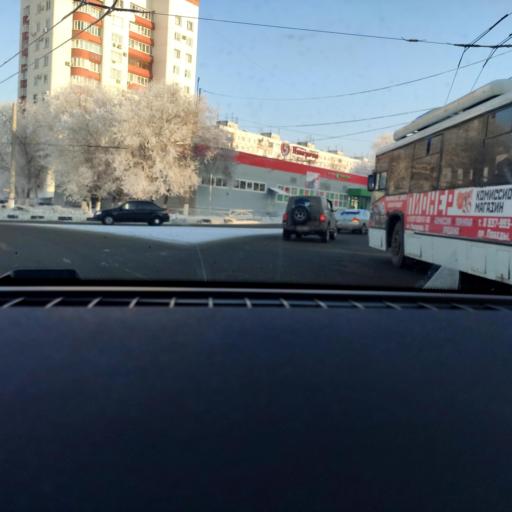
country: RU
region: Samara
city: Novokuybyshevsk
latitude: 53.0957
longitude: 49.9713
